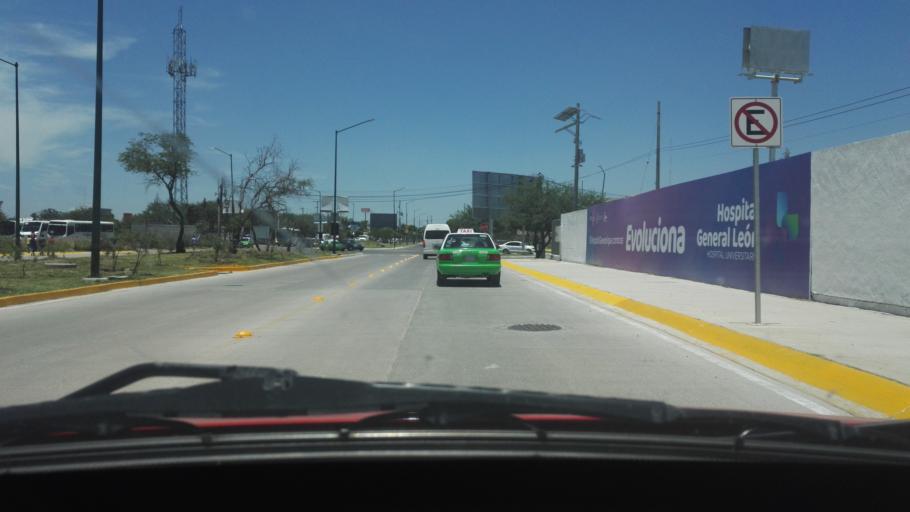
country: MX
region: Guanajuato
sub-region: Leon
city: Ladrilleras del Refugio
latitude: 21.0606
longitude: -101.5737
